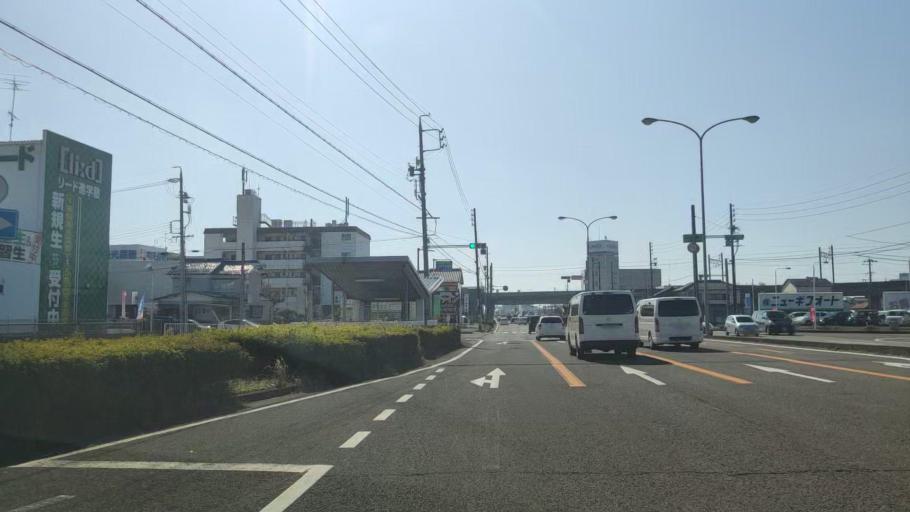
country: JP
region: Gifu
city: Gifu-shi
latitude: 35.4033
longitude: 136.7848
